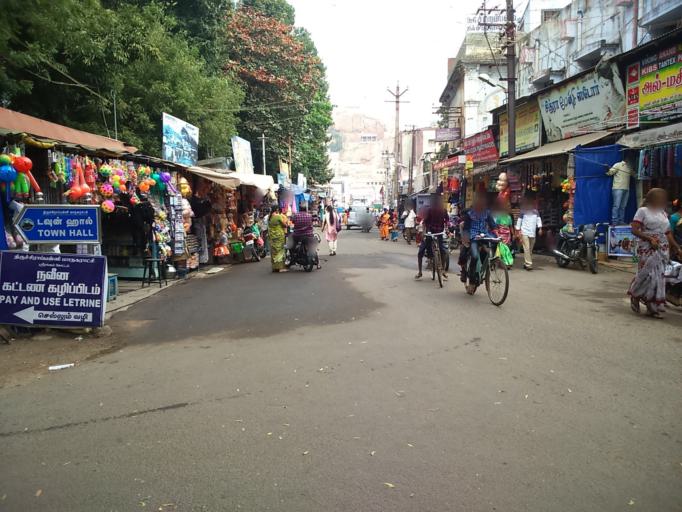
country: IN
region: Tamil Nadu
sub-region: Tiruchchirappalli
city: Tiruchirappalli
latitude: 10.8248
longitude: 78.6971
